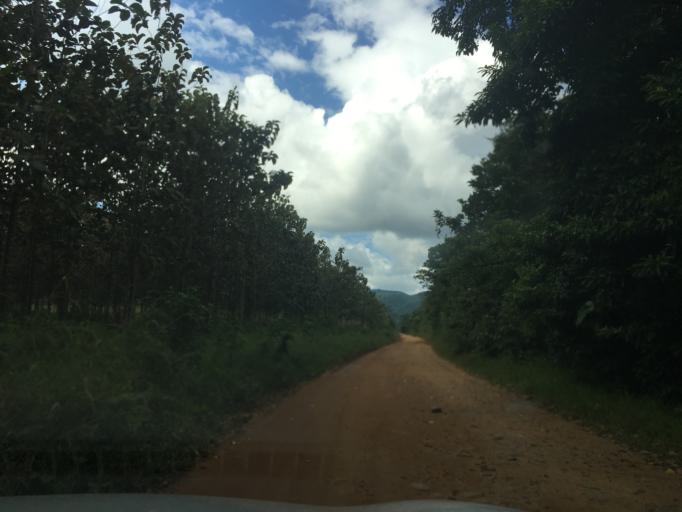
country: BZ
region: Stann Creek
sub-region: Dangriga
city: Dangriga
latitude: 16.9366
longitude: -88.3580
